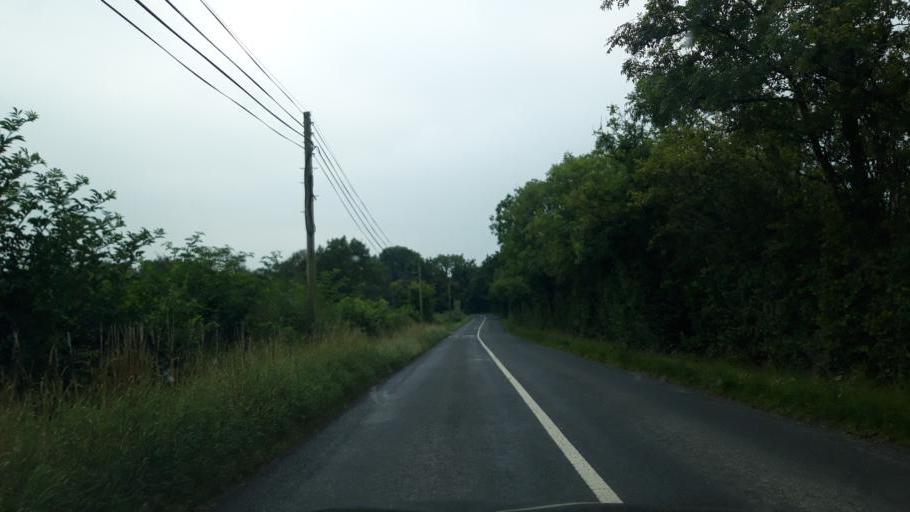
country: IE
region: Munster
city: Fethard
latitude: 52.5287
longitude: -7.6804
